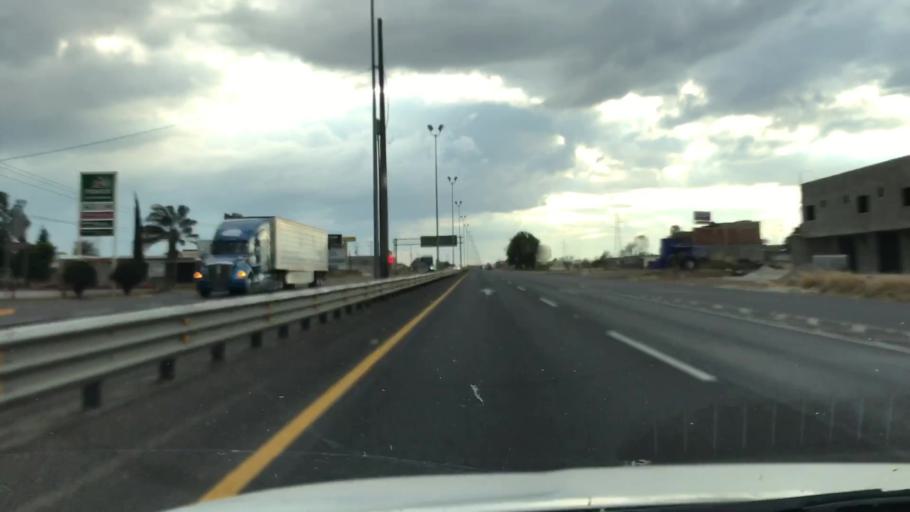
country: MX
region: Guanajuato
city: Penjamo
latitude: 20.4335
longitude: -101.7010
